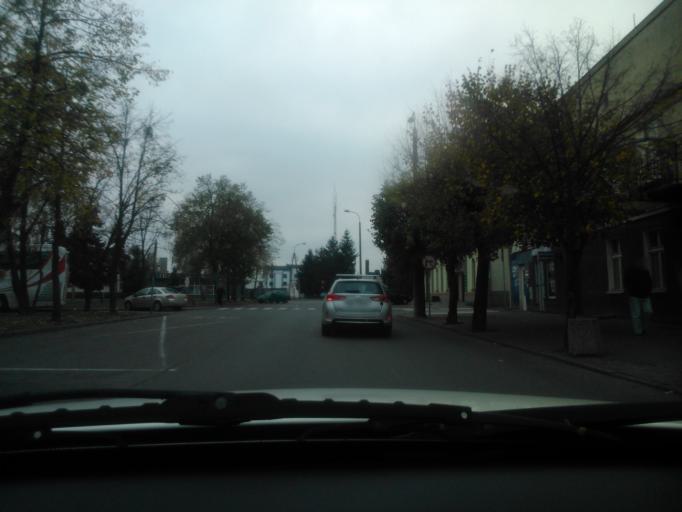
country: PL
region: Kujawsko-Pomorskie
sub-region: Powiat golubsko-dobrzynski
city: Golub-Dobrzyn
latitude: 53.1095
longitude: 19.0524
